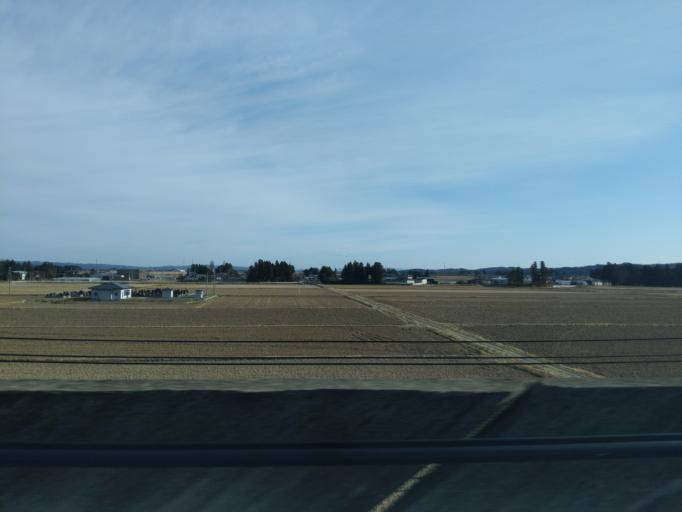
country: JP
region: Miyagi
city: Furukawa
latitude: 38.5337
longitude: 140.9609
